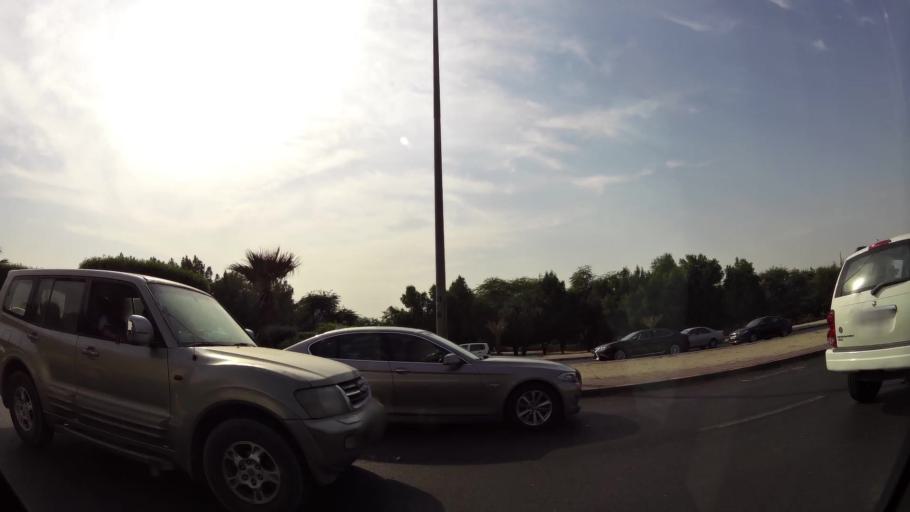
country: KW
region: Al Farwaniyah
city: Al Farwaniyah
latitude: 29.3000
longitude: 47.9642
